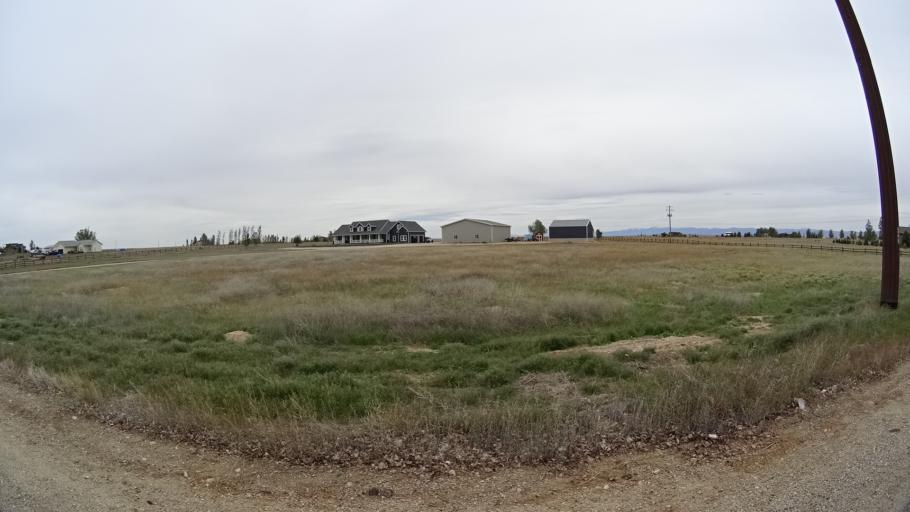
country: US
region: Idaho
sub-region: Ada County
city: Kuna
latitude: 43.4885
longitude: -116.2994
